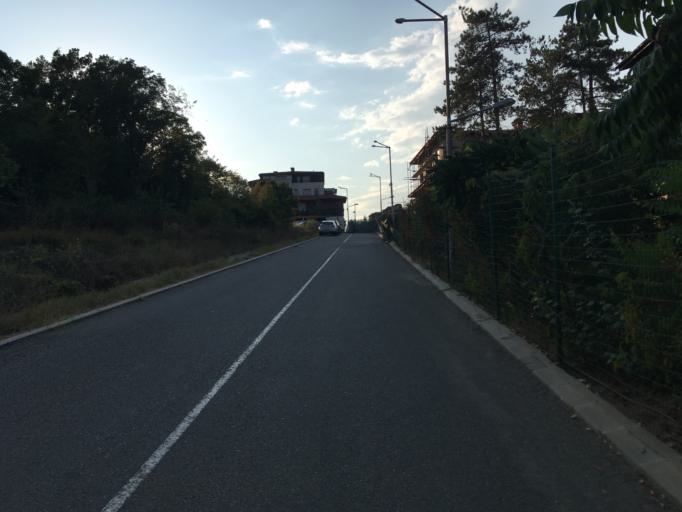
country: BG
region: Burgas
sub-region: Obshtina Sozopol
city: Sozopol
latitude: 42.4108
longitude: 27.6826
